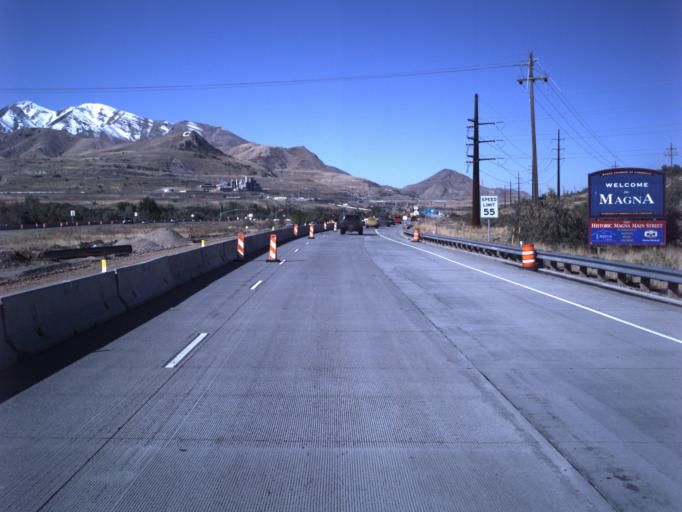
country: US
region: Utah
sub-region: Salt Lake County
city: Magna
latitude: 40.7183
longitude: -112.0838
